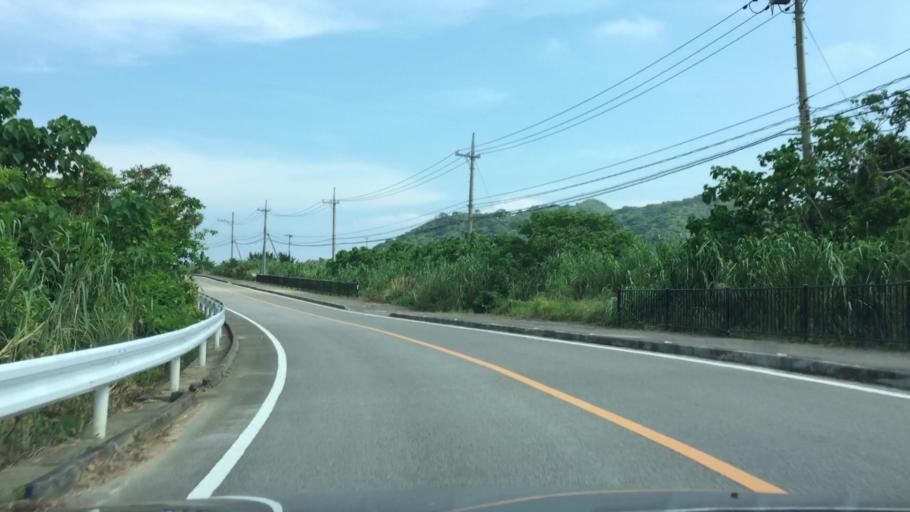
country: JP
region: Okinawa
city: Ishigaki
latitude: 24.5080
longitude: 124.2700
